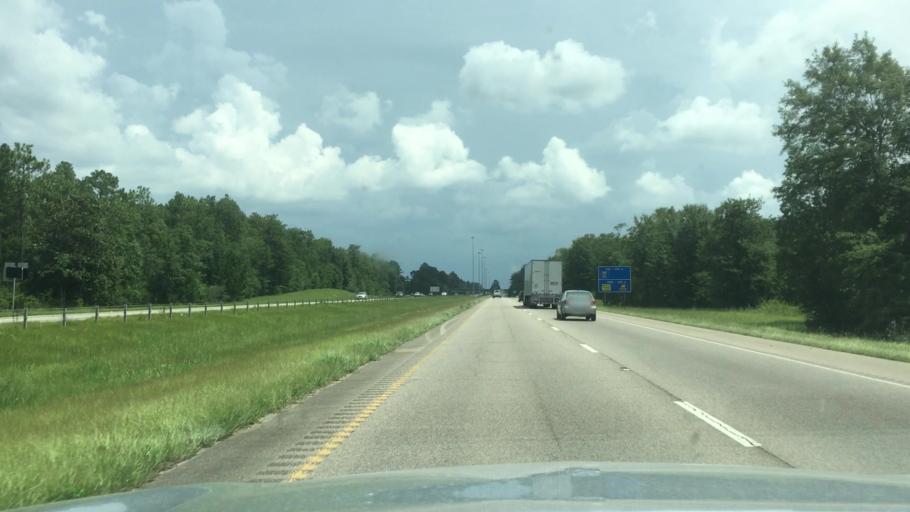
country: US
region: Mississippi
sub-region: Pearl River County
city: Picayune
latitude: 30.5362
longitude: -89.6535
